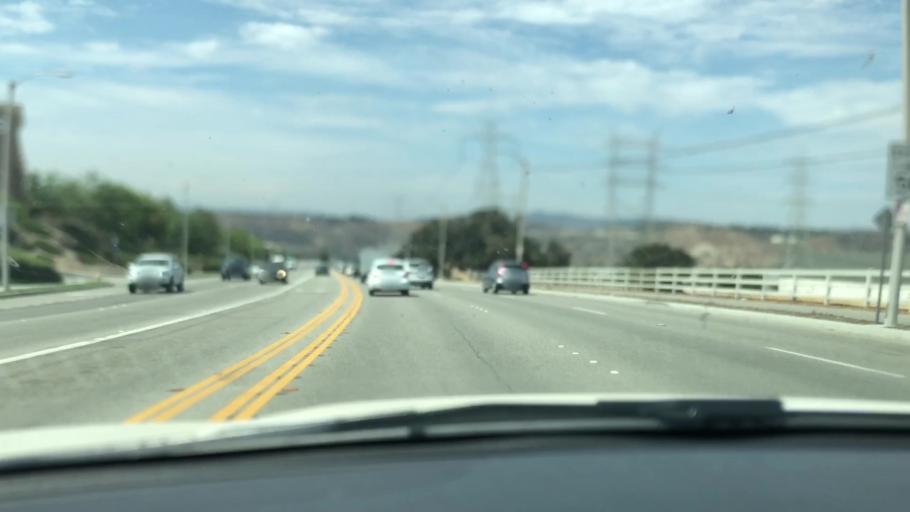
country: US
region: California
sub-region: Los Angeles County
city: Santa Clarita
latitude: 34.4131
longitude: -118.5021
